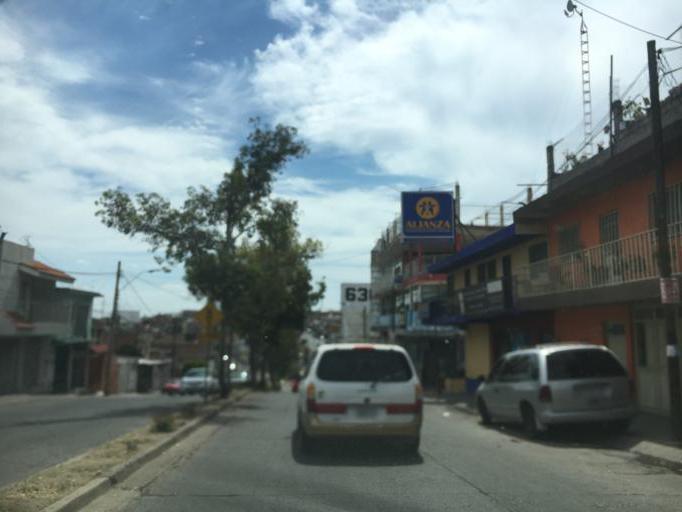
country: MX
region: Guanajuato
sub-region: Leon
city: La Ermita
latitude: 21.1437
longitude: -101.7020
